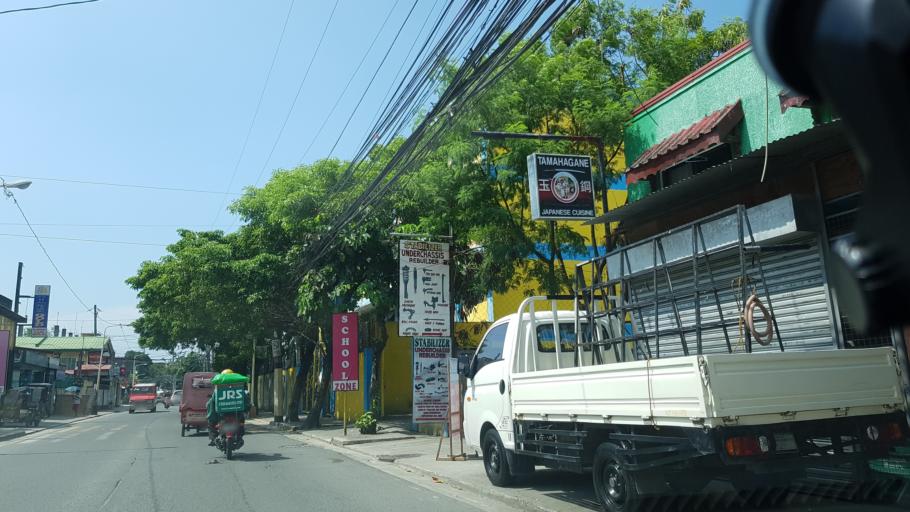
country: PH
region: Calabarzon
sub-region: Province of Rizal
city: Las Pinas
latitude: 14.4666
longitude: 120.9828
